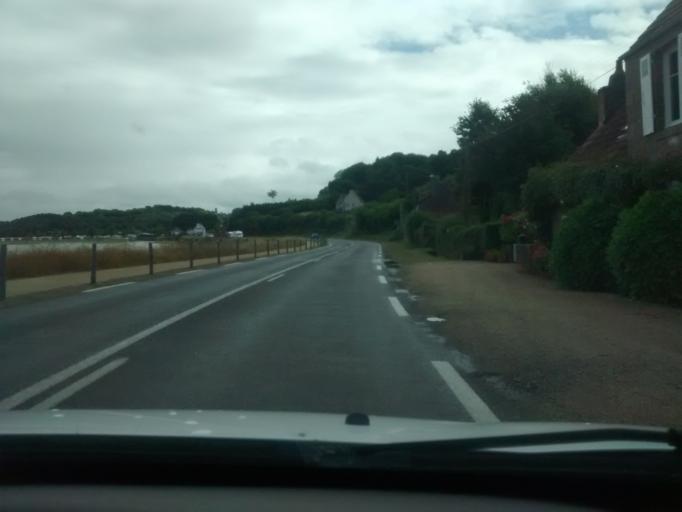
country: FR
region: Brittany
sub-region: Departement des Cotes-d'Armor
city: Perros-Guirec
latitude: 48.7978
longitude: -3.4369
